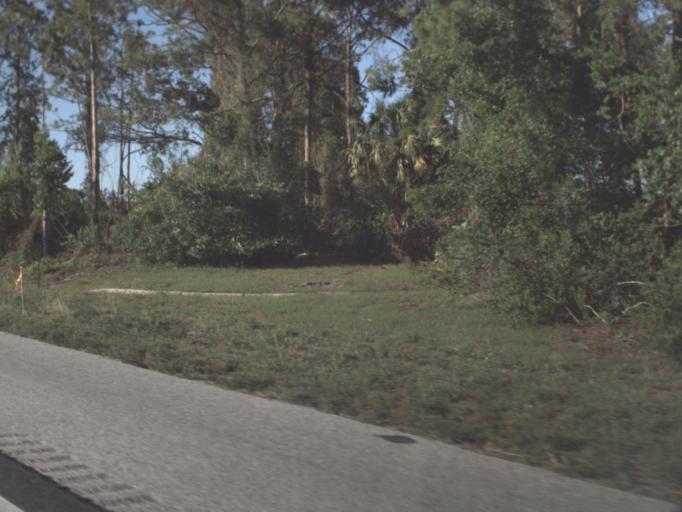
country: US
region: Florida
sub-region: Flagler County
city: Flagler Beach
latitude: 29.4205
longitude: -81.1623
